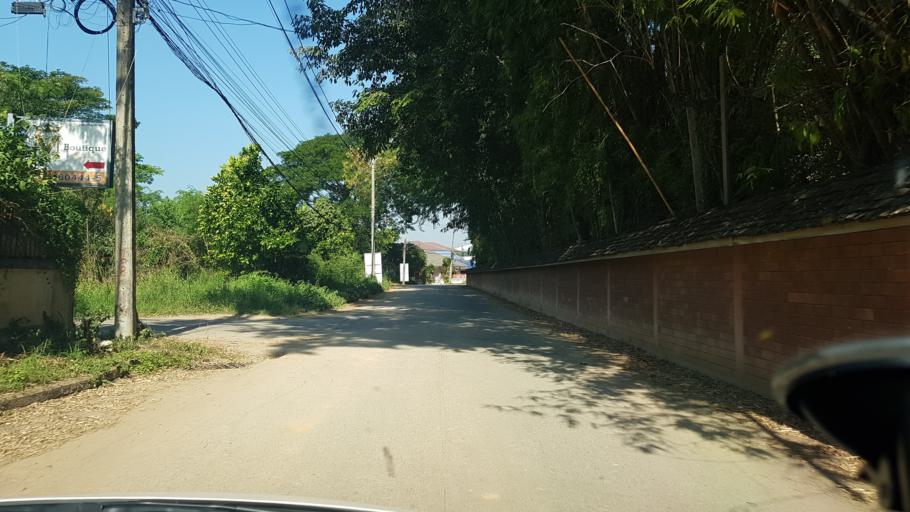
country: TH
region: Chiang Rai
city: Chiang Rai
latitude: 19.9029
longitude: 99.7933
